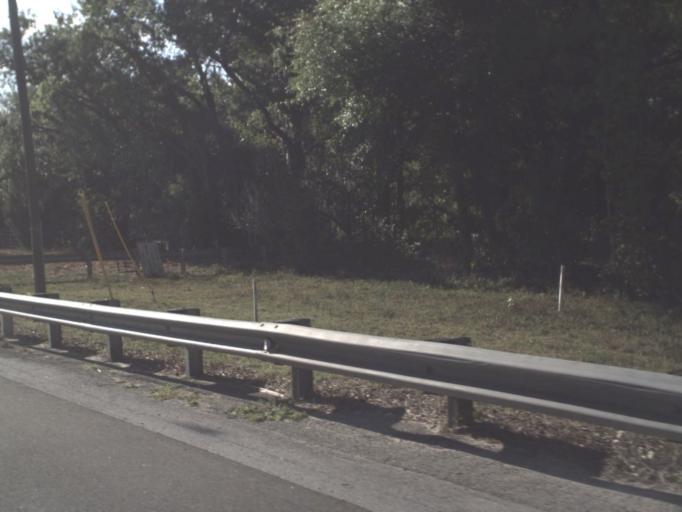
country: US
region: Florida
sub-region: Seminole County
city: Heathrow
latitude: 28.8153
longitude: -81.4221
